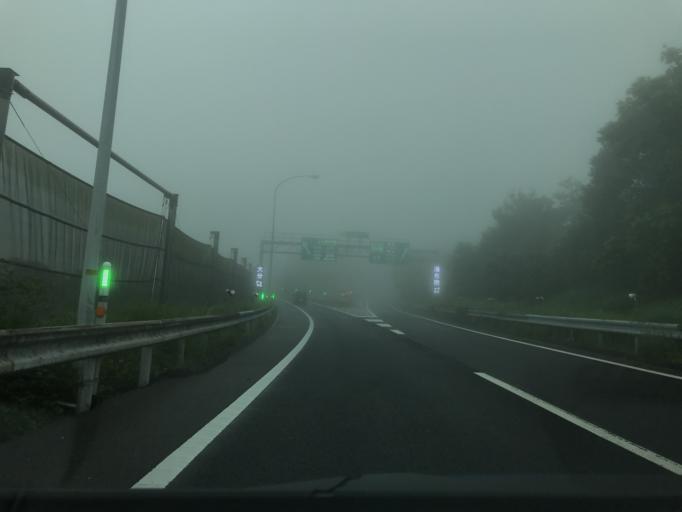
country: JP
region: Oita
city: Hiji
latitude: 33.3537
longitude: 131.4470
